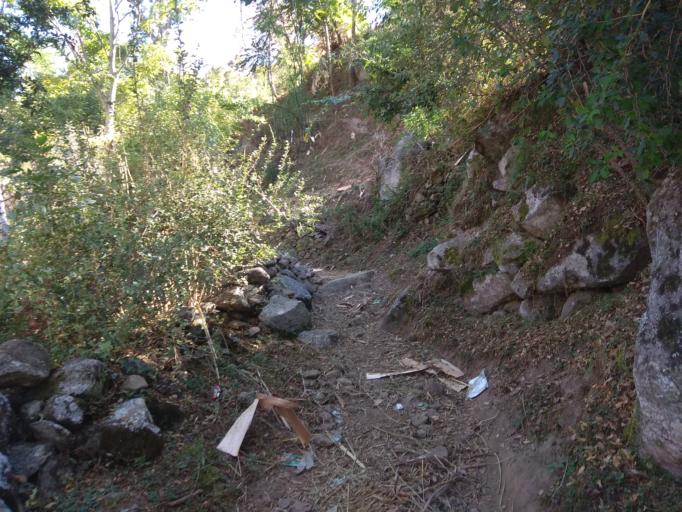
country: NP
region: Far Western
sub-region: Seti Zone
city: Achham
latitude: 29.2391
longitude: 81.6353
